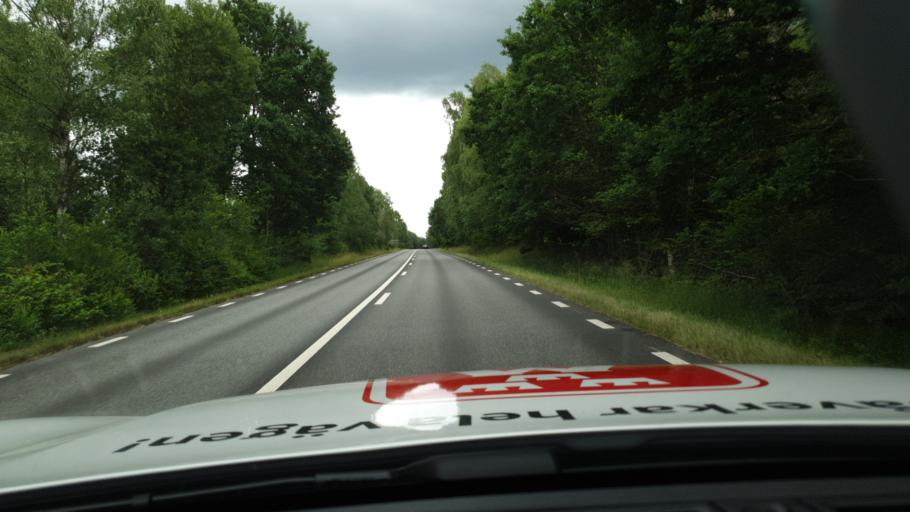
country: SE
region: Skane
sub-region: Hassleholms Kommun
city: Tormestorp
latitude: 56.1107
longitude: 13.7318
